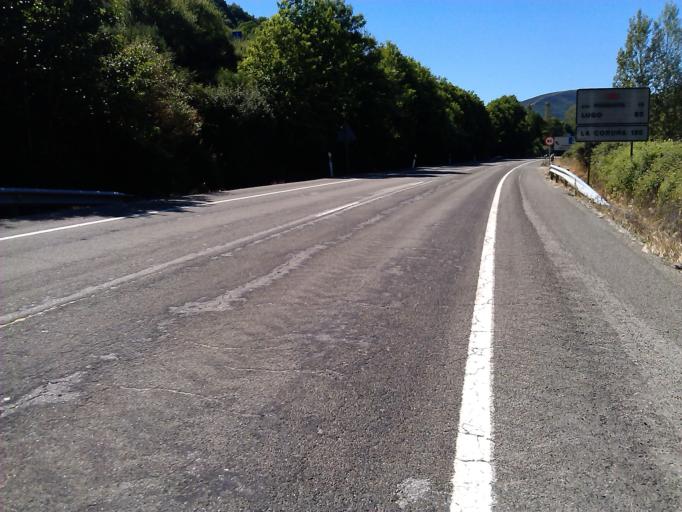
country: ES
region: Castille and Leon
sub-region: Provincia de Leon
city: Trabadelo
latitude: 42.6408
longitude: -6.8685
